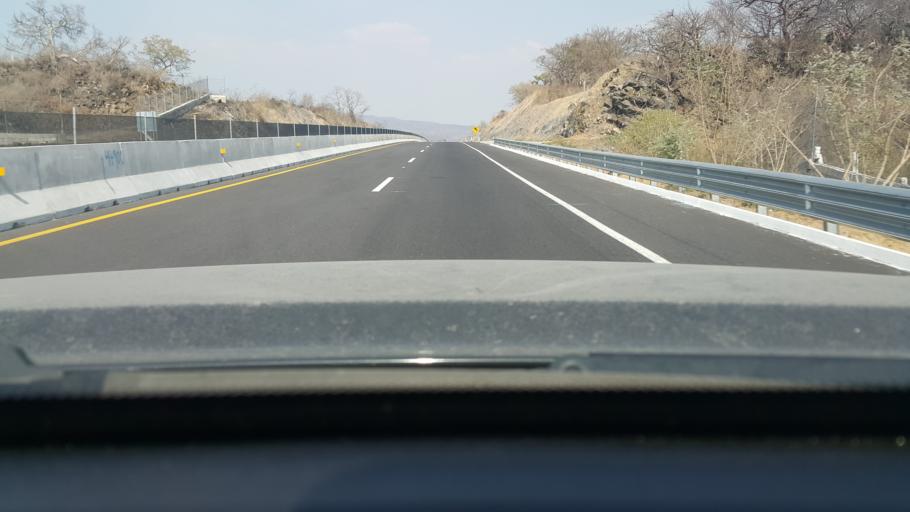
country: MX
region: Nayarit
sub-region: Ahuacatlan
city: Ahuacatlan
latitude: 21.0670
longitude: -104.4699
